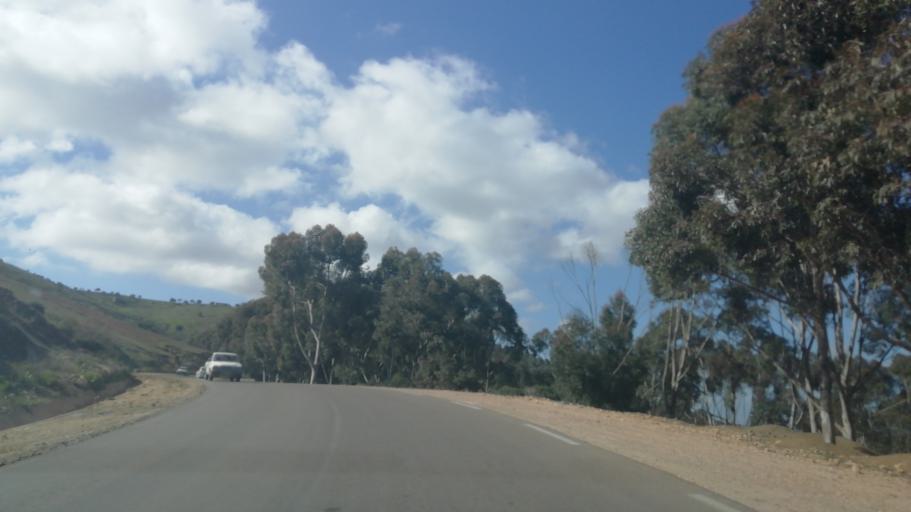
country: DZ
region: Relizane
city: Relizane
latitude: 36.0840
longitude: 0.4779
